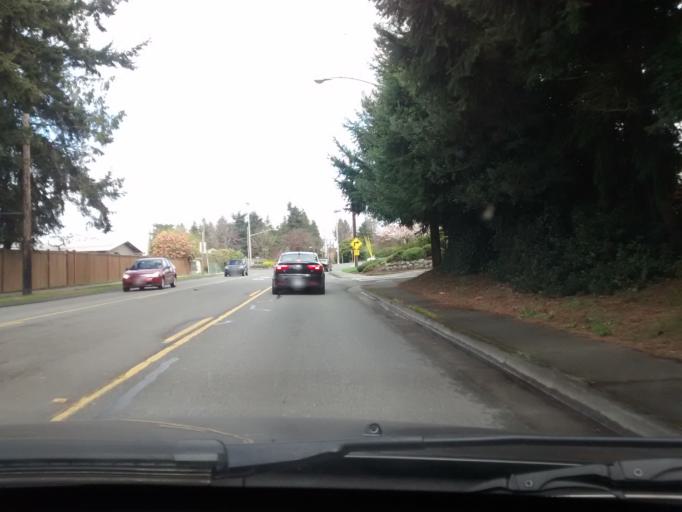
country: US
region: Washington
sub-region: Snohomish County
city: Edmonds
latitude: 47.8203
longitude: -122.3670
